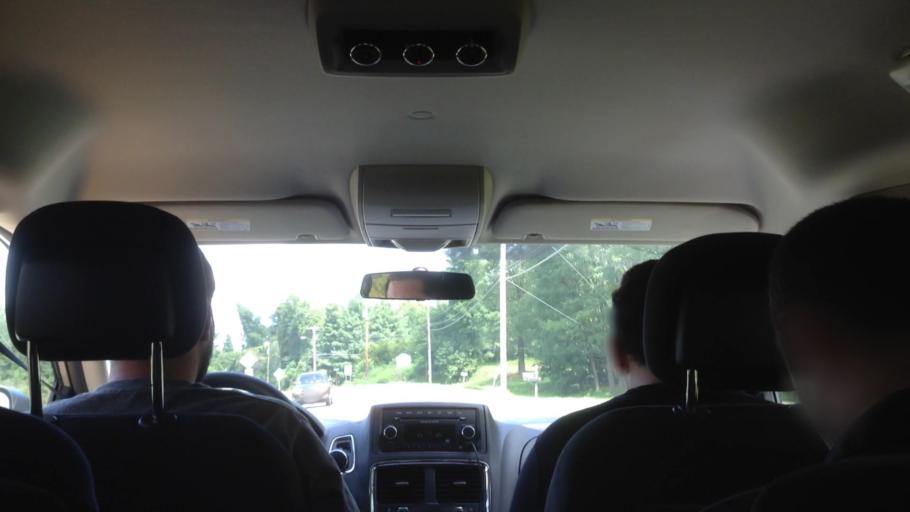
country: US
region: New York
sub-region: Dutchess County
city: Red Hook
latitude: 42.0200
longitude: -73.8505
